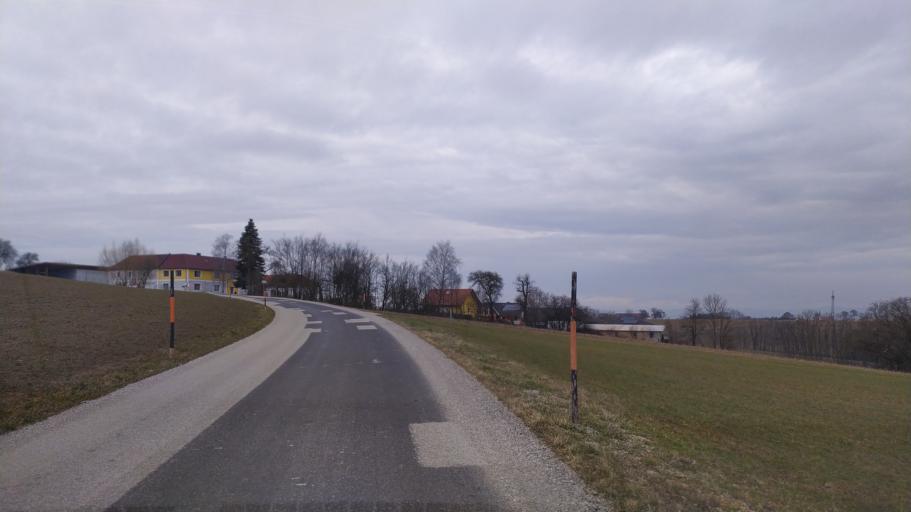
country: AT
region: Lower Austria
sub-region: Politischer Bezirk Amstetten
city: Strengberg
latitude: 48.1355
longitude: 14.7170
